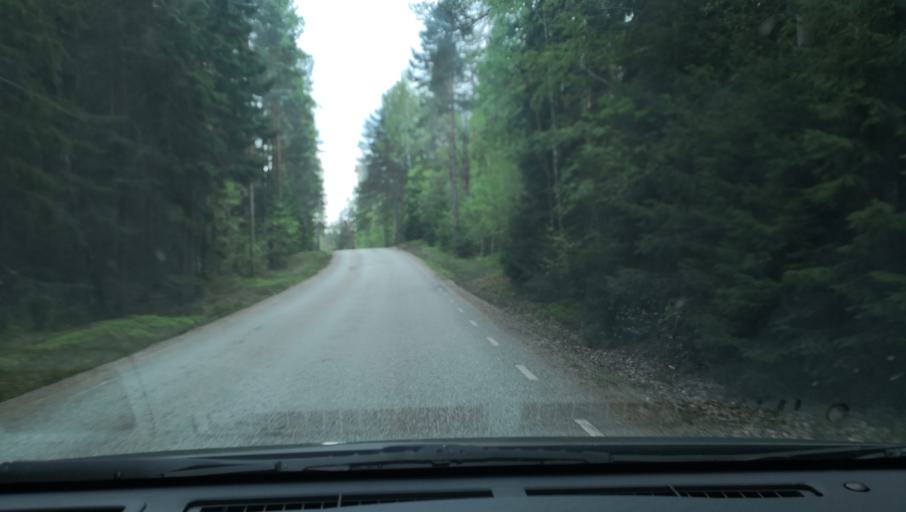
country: SE
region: Vaestmanland
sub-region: Skinnskattebergs Kommun
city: Skinnskatteberg
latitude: 59.8259
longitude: 15.5527
